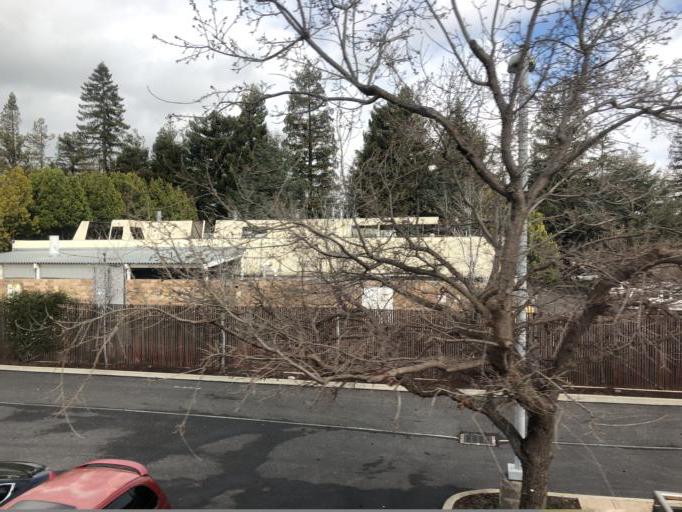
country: US
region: California
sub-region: Santa Clara County
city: Sunnyvale
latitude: 37.3707
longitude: -121.9980
